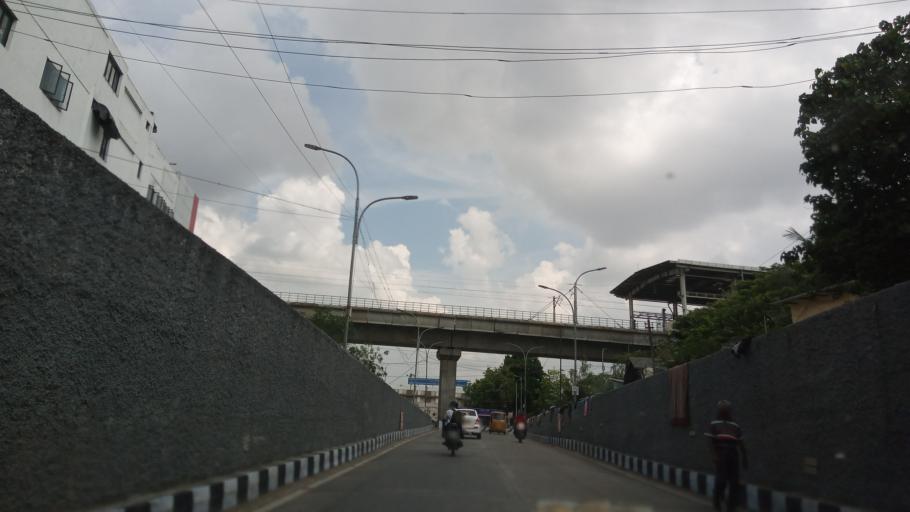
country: IN
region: Tamil Nadu
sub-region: Kancheepuram
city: Manappakkam
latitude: 12.9865
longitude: 80.1763
